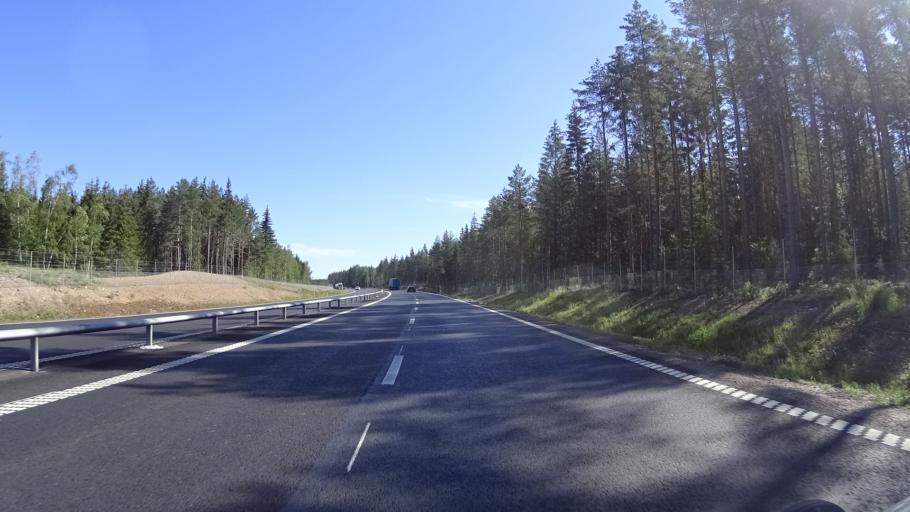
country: SE
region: Vaestra Goetaland
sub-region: Gullspangs Kommun
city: Hova
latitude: 58.8372
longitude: 14.1876
